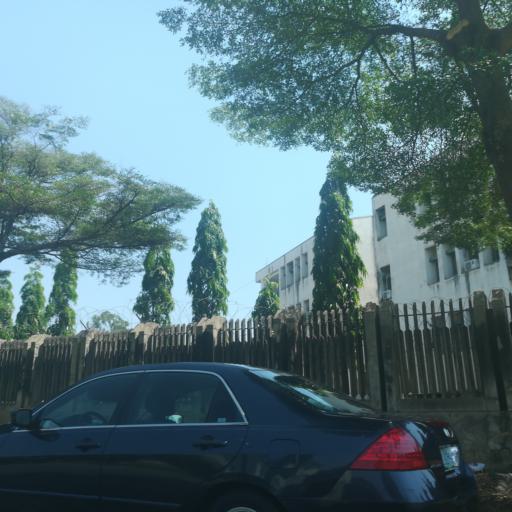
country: NG
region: Abuja Federal Capital Territory
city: Abuja
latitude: 9.0759
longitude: 7.4500
